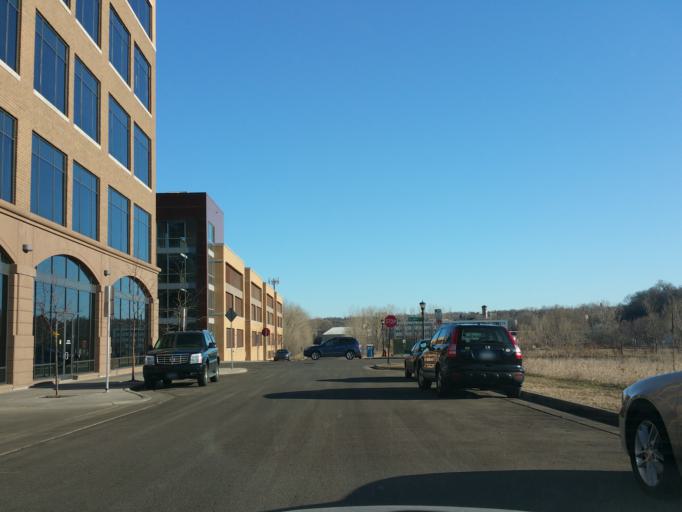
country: US
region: Minnesota
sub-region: Ramsey County
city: Saint Paul
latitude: 44.9414
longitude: -93.0866
